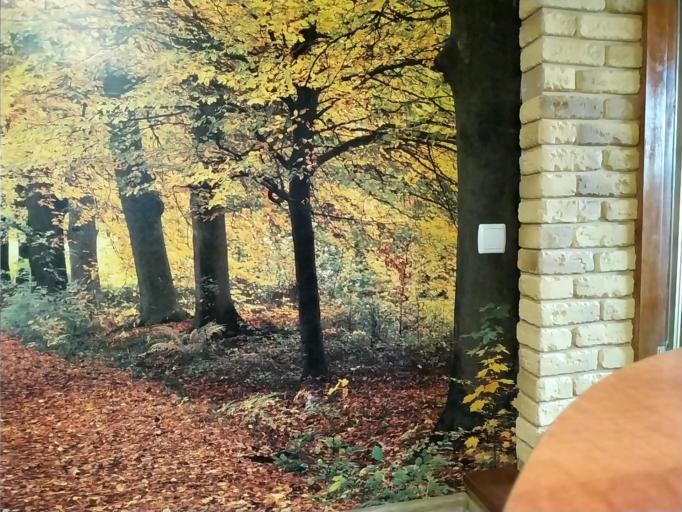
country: RU
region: Leningrad
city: Tolmachevo
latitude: 58.9373
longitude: 29.6884
